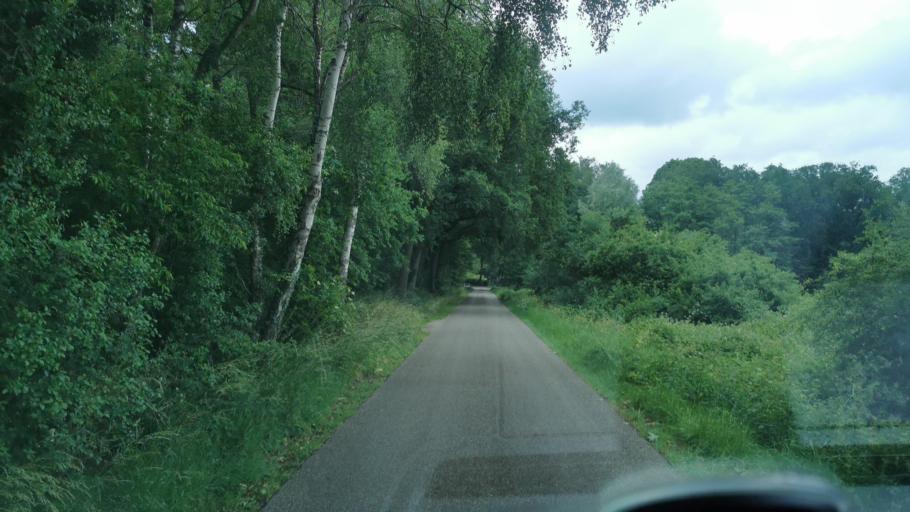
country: NL
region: Overijssel
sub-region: Gemeente Losser
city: Losser
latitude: 52.2576
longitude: 6.9562
